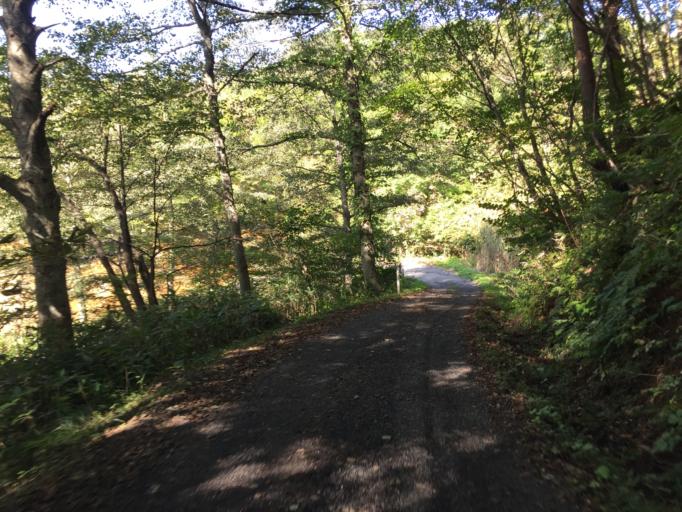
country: JP
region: Yamagata
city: Yonezawa
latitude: 37.8226
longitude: 140.2357
